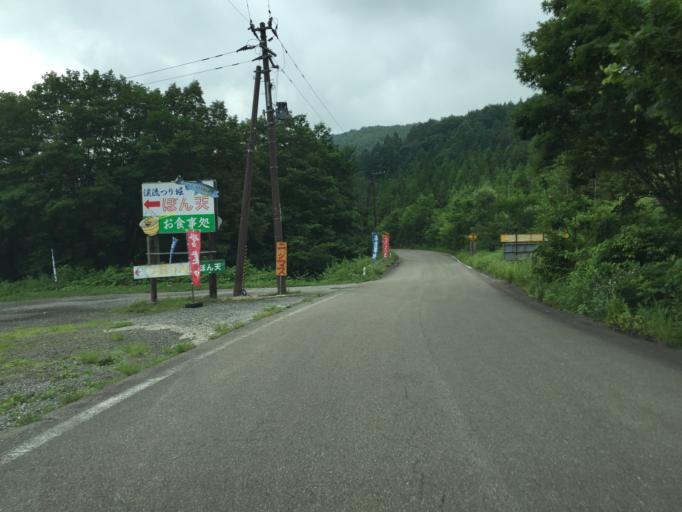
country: JP
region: Fukushima
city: Inawashiro
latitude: 37.6473
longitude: 140.2229
